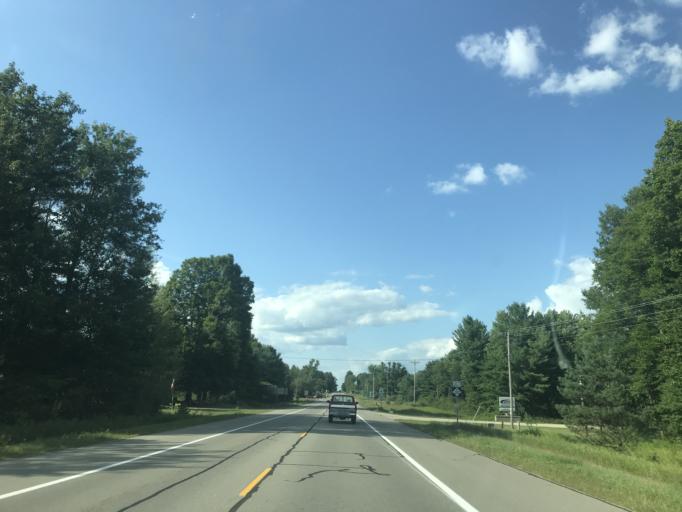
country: US
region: Michigan
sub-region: Newaygo County
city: White Cloud
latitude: 43.5659
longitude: -85.7715
